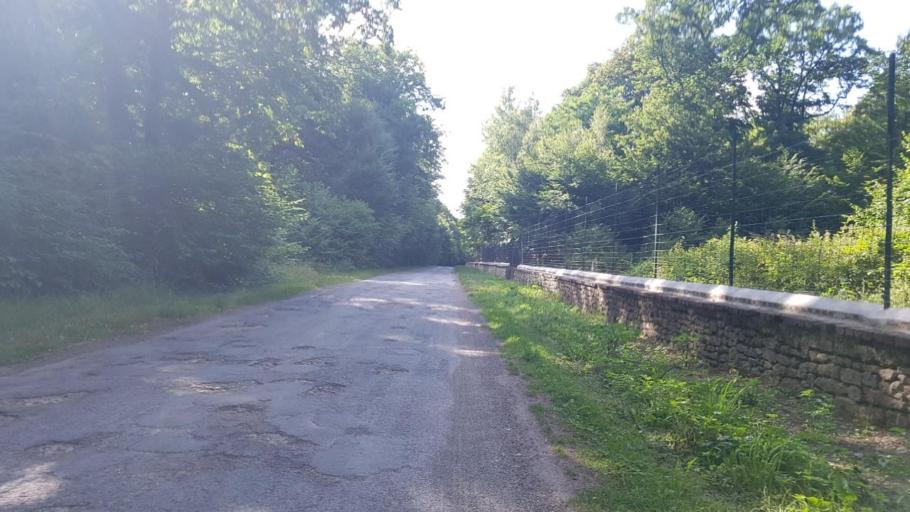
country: FR
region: Picardie
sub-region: Departement de l'Oise
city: Senlis
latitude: 49.1850
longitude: 2.6110
